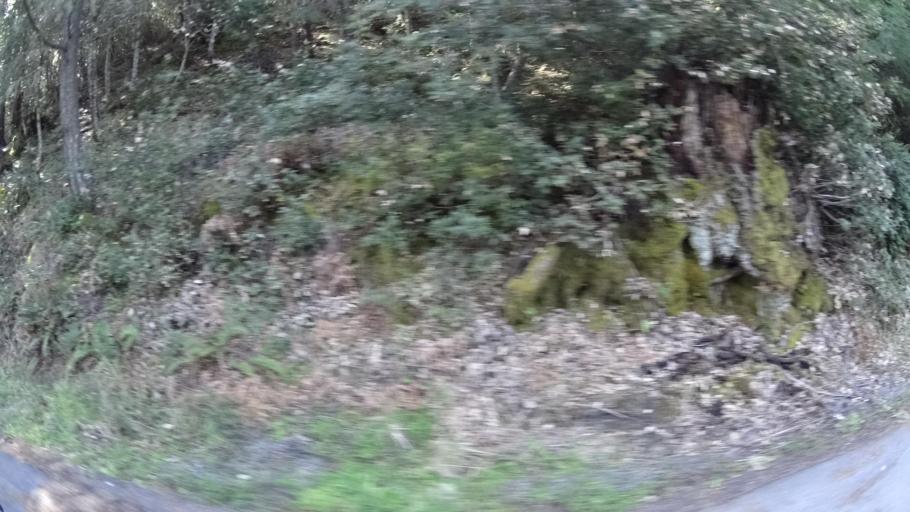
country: US
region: California
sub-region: Humboldt County
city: Redway
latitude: 40.0762
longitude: -123.6539
